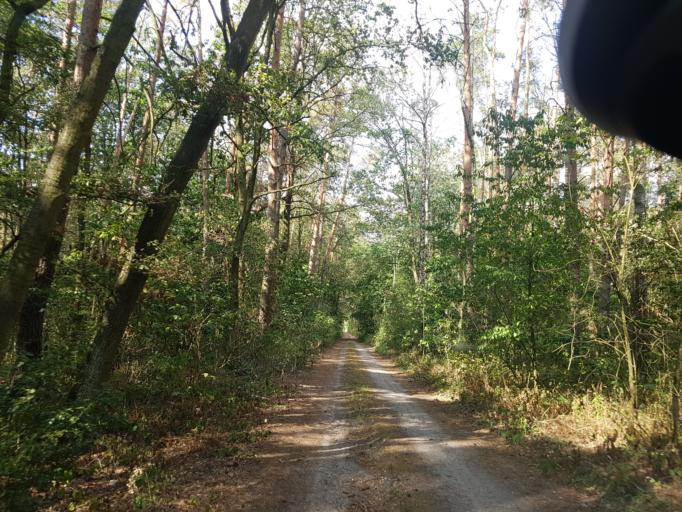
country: DE
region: Brandenburg
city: Calau
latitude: 51.7627
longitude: 13.9517
